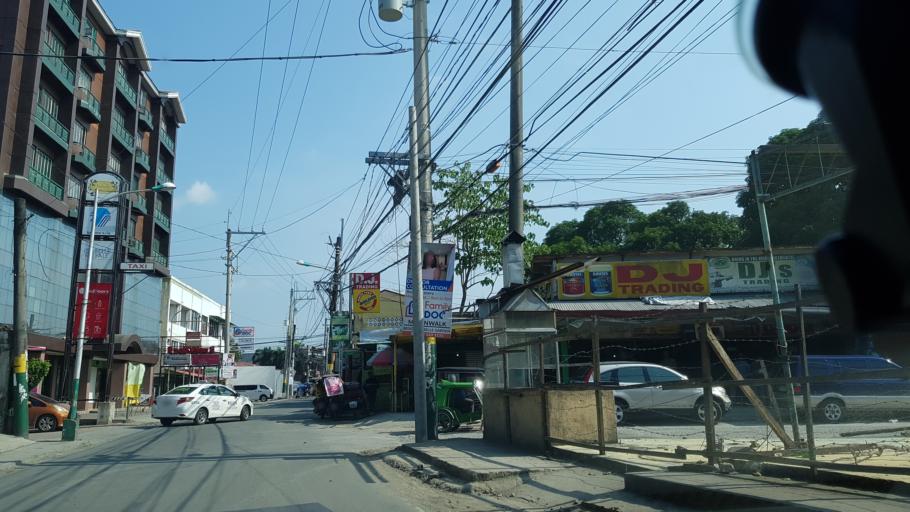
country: PH
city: Sambayanihan People's Village
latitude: 14.4954
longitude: 121.0140
